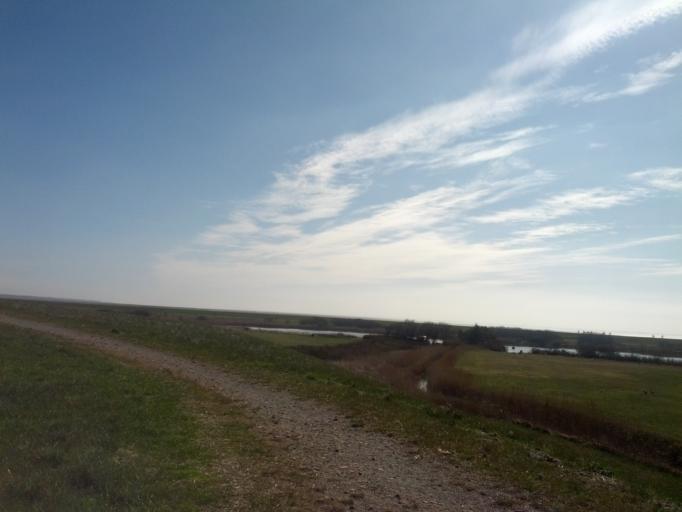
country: DE
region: Lower Saxony
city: Langeoog
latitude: 53.7449
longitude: 7.5009
